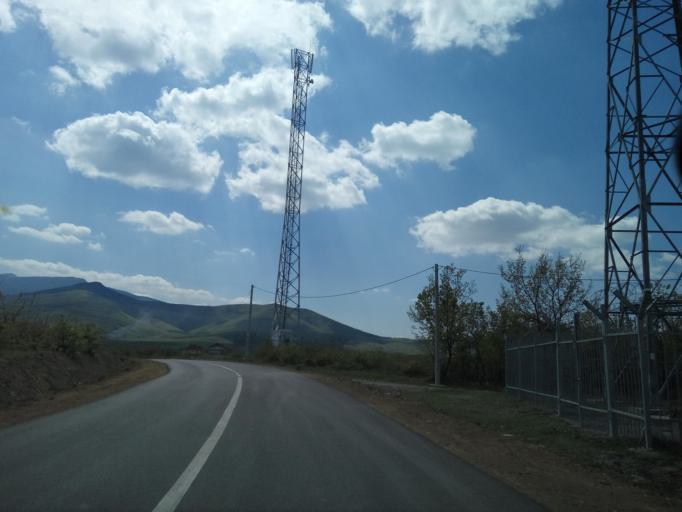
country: XK
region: Gjakova
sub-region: Komuna e Gjakoves
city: Gjakove
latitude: 42.3366
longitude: 20.4648
